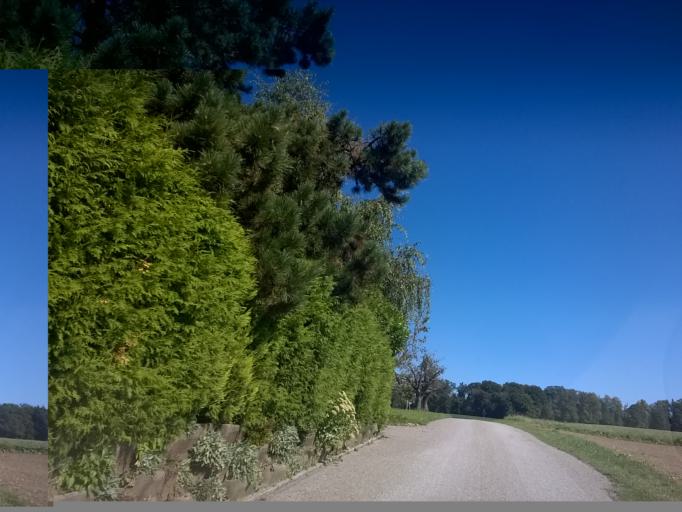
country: CH
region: Zurich
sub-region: Bezirk Buelach
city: Rorbas
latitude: 47.5195
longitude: 8.5687
